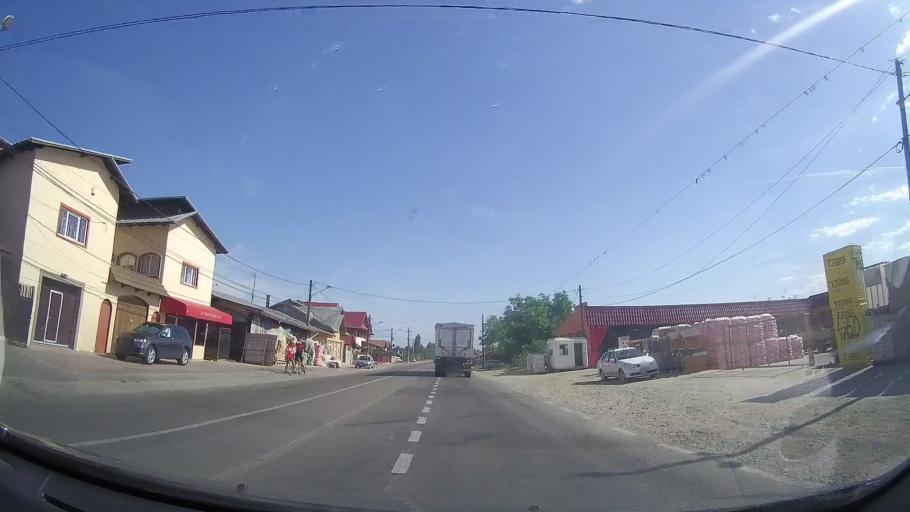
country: RO
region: Prahova
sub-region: Comuna Lipanesti
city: Sipotu
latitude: 45.0301
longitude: 26.0182
